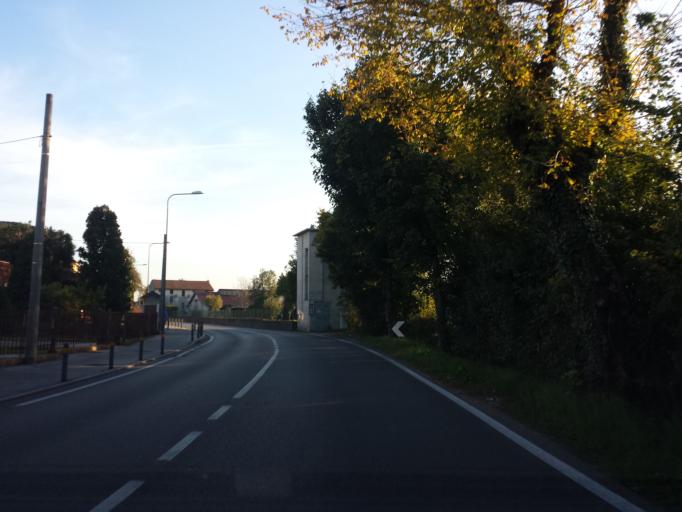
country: IT
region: Veneto
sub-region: Provincia di Vicenza
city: Vicenza
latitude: 45.5782
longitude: 11.5349
